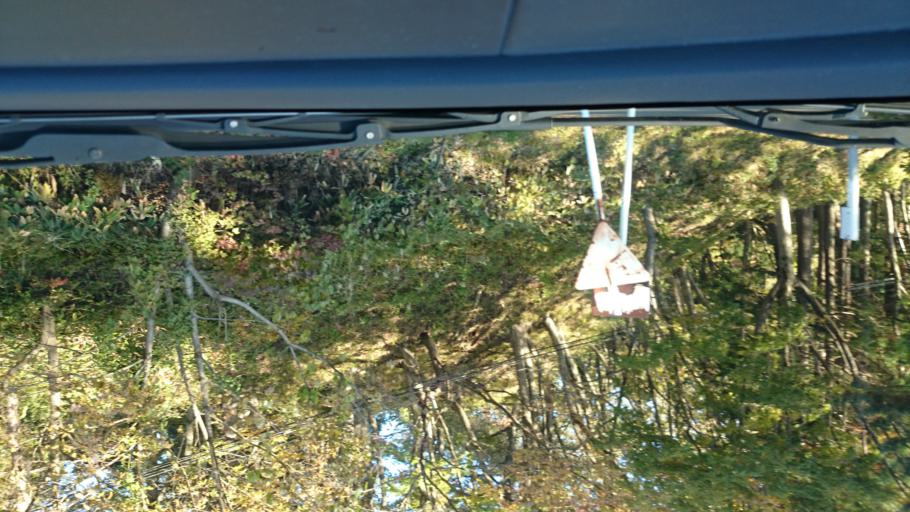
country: JP
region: Fukushima
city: Kitakata
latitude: 37.4562
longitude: 139.5835
